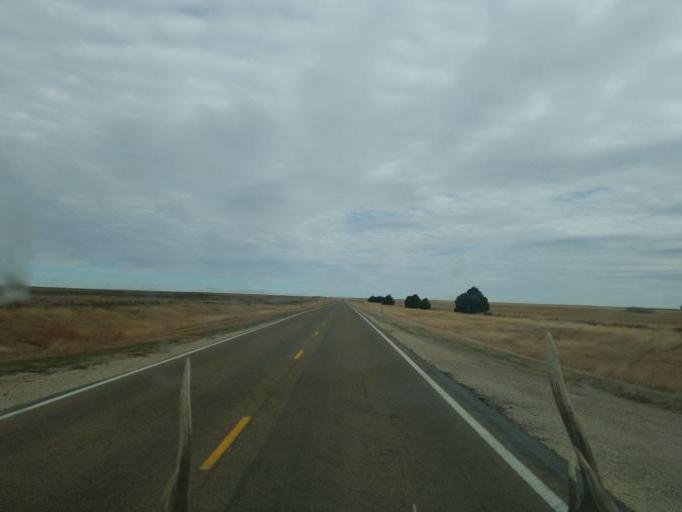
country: US
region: Kansas
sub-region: Wallace County
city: Sharon Springs
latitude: 39.0249
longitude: -101.3228
